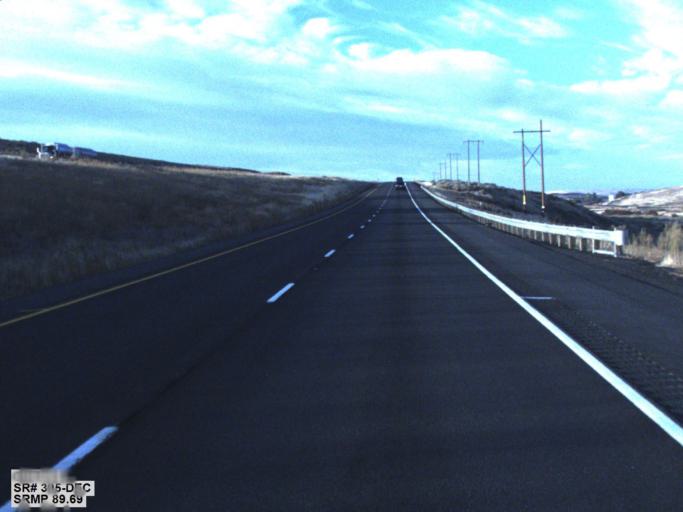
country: US
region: Washington
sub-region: Adams County
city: Ritzville
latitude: 47.0403
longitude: -118.4522
